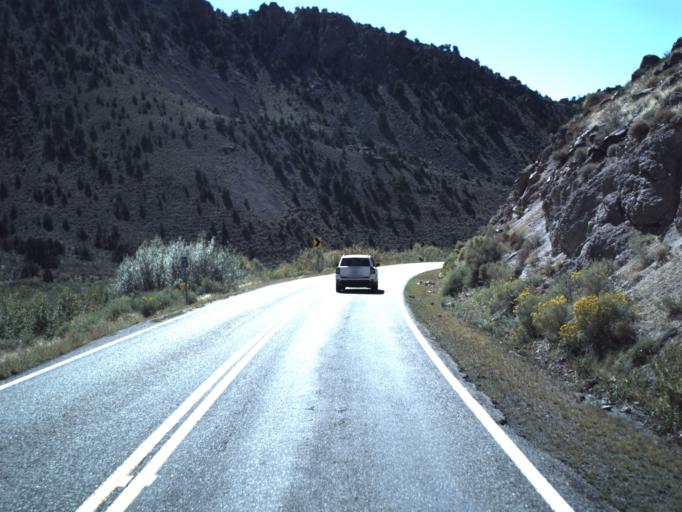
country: US
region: Utah
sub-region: Piute County
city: Junction
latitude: 38.1945
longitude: -112.1269
